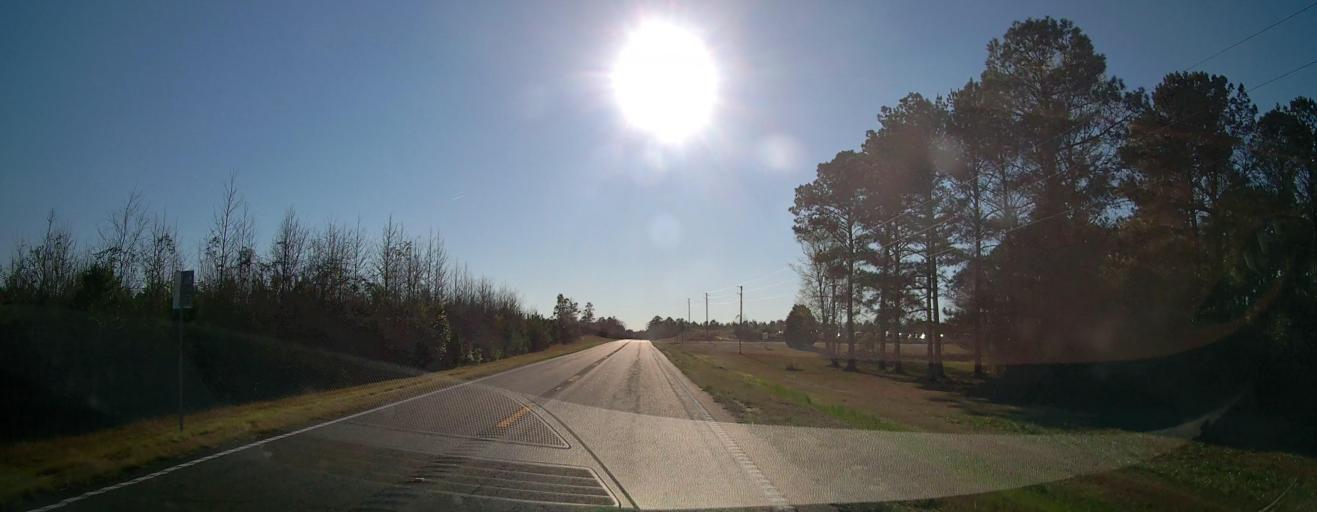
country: US
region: Georgia
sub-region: Taylor County
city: Butler
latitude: 32.5524
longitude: -84.2684
